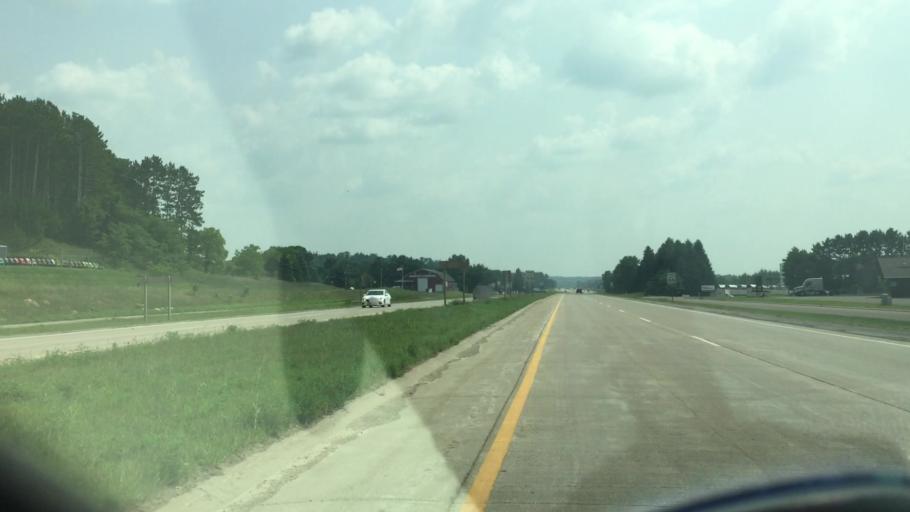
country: US
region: Wisconsin
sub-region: Eau Claire County
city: Altoona
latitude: 44.7600
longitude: -91.4576
